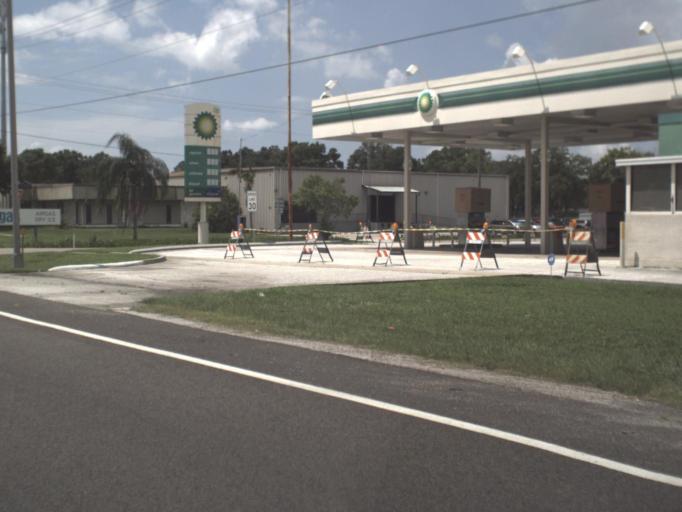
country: US
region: Florida
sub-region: Hillsborough County
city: East Lake-Orient Park
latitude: 27.9710
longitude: -82.3605
